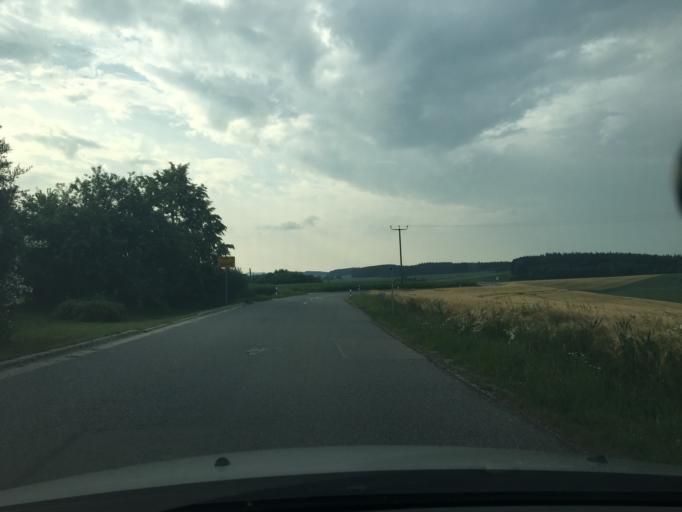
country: DE
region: Bavaria
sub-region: Upper Bavaria
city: Egglkofen
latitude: 48.3785
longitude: 12.4283
